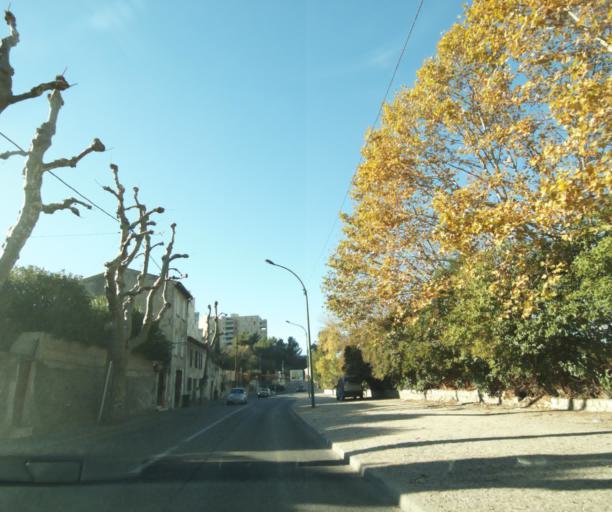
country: FR
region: Provence-Alpes-Cote d'Azur
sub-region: Departement des Bouches-du-Rhone
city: La Penne-sur-Huveaune
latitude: 43.2822
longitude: 5.5090
